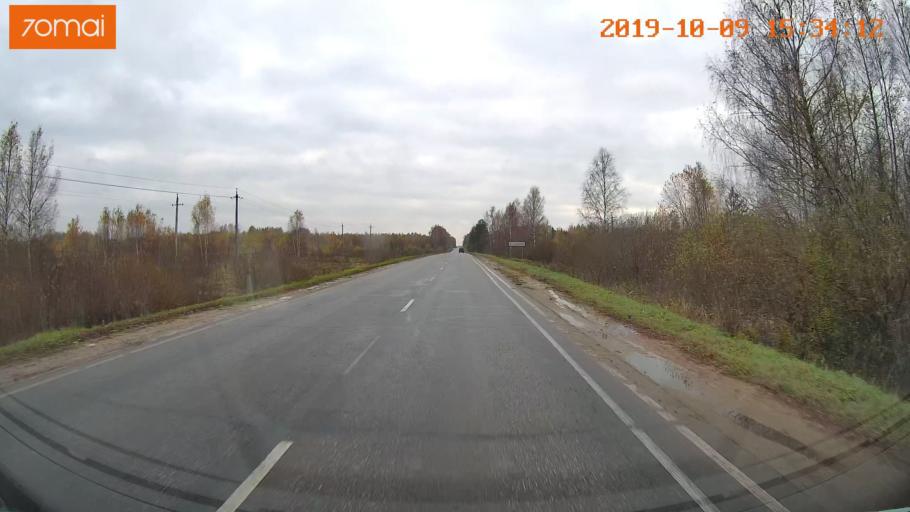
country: RU
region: Kostroma
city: Oktyabr'skiy
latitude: 57.9428
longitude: 41.2488
